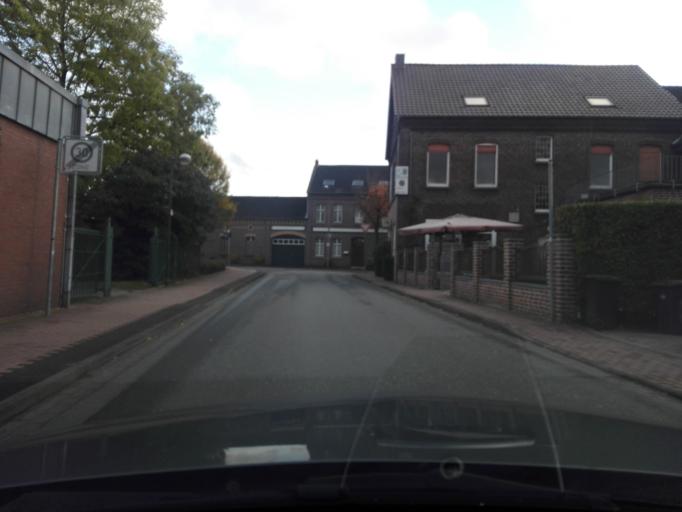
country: DE
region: North Rhine-Westphalia
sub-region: Regierungsbezirk Dusseldorf
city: Wachtendonk
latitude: 51.4573
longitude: 6.3759
